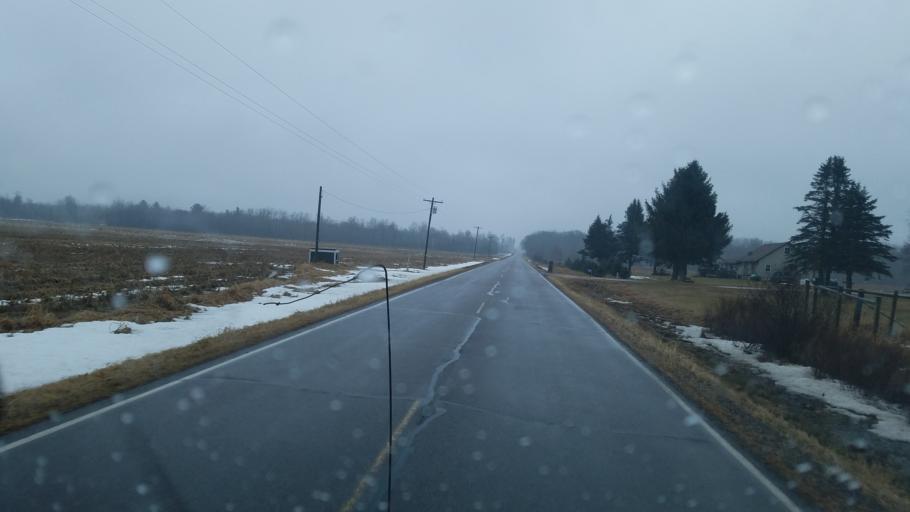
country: US
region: Wisconsin
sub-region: Wood County
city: Marshfield
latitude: 44.4857
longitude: -90.2797
